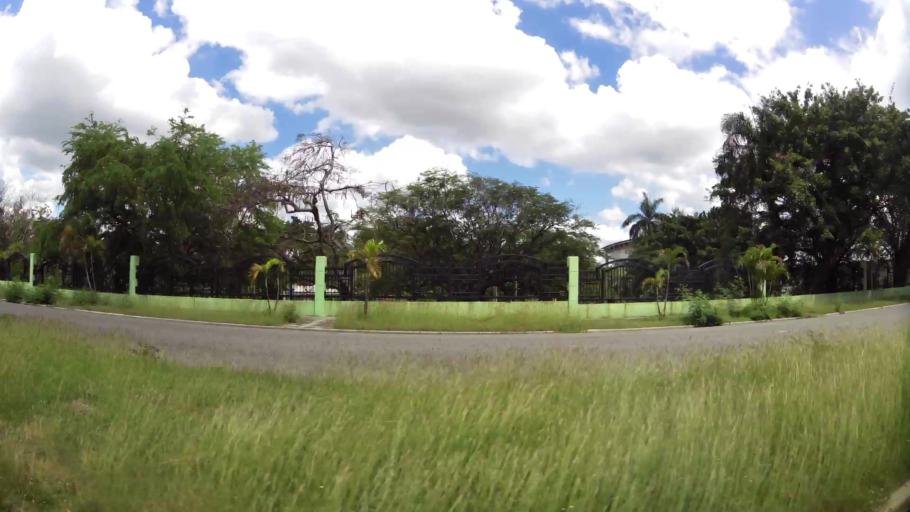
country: DO
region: Santo Domingo
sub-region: Santo Domingo
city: Santo Domingo Este
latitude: 18.4779
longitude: -69.8573
